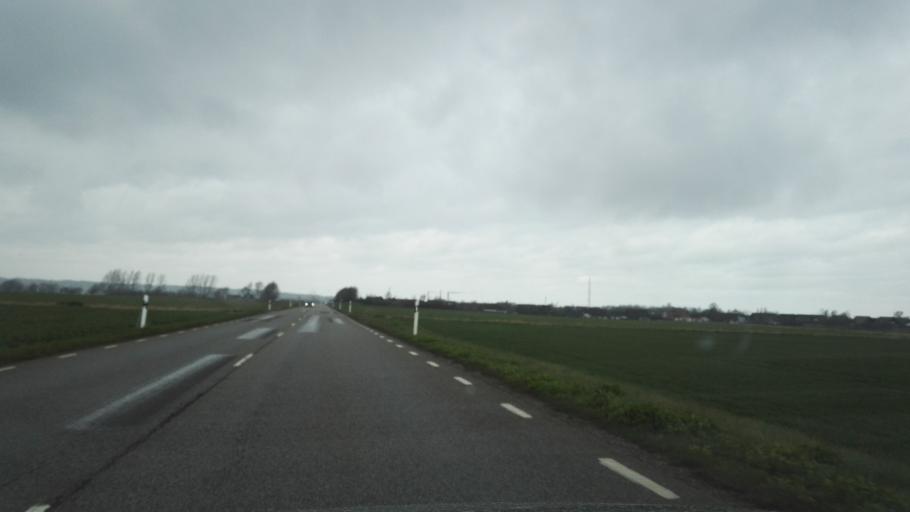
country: SE
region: Skane
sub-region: Simrishamns Kommun
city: Simrishamn
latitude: 55.5359
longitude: 14.3396
